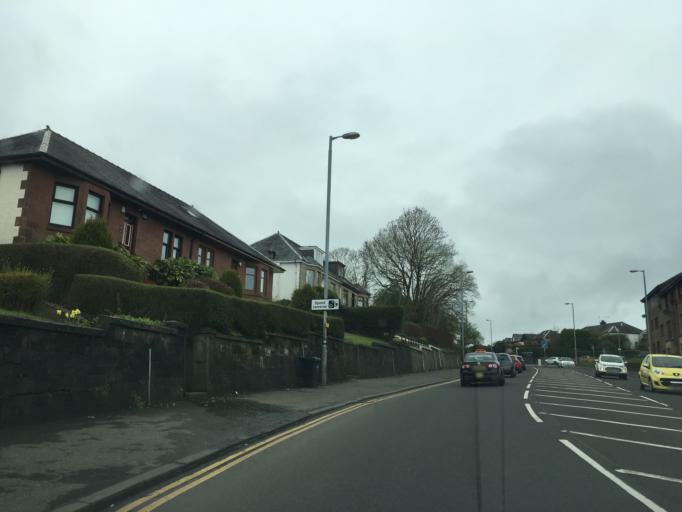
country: GB
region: Scotland
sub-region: Inverclyde
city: Greenock
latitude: 55.9402
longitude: -4.7896
